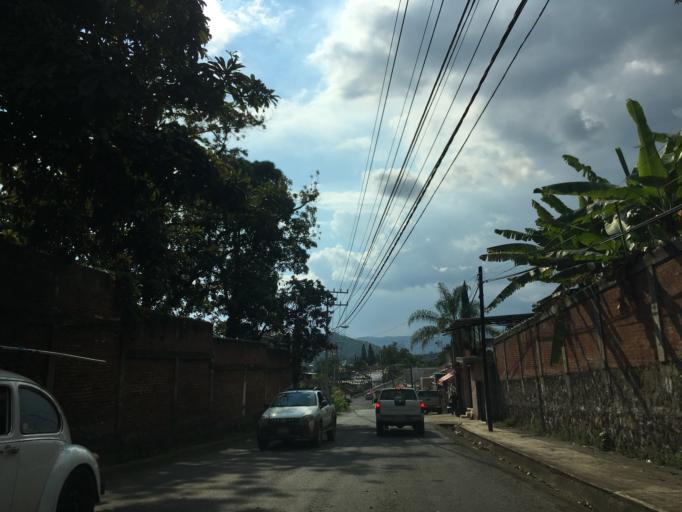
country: MX
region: Michoacan
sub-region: Ziracuaretiro
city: Patuan
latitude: 19.4174
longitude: -101.9060
